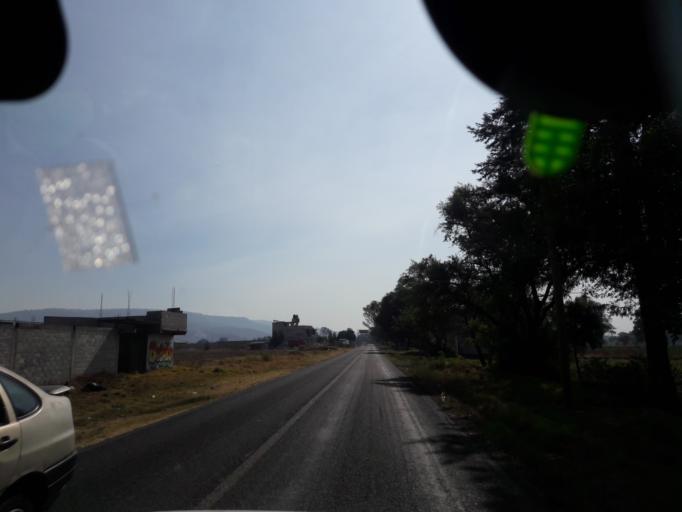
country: MX
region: Tlaxcala
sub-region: Ixtacuixtla de Mariano Matamoros
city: Santa Justina Ecatepec
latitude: 19.3145
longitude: -98.3304
